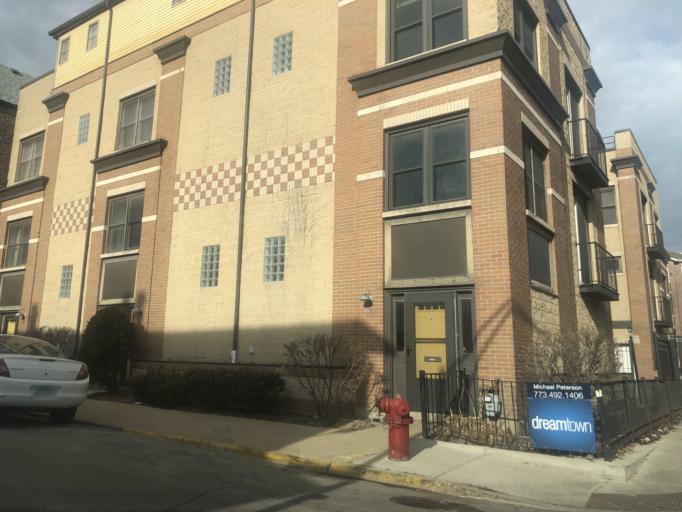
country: US
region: Illinois
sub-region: Cook County
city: Chicago
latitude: 41.8976
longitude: -87.6649
